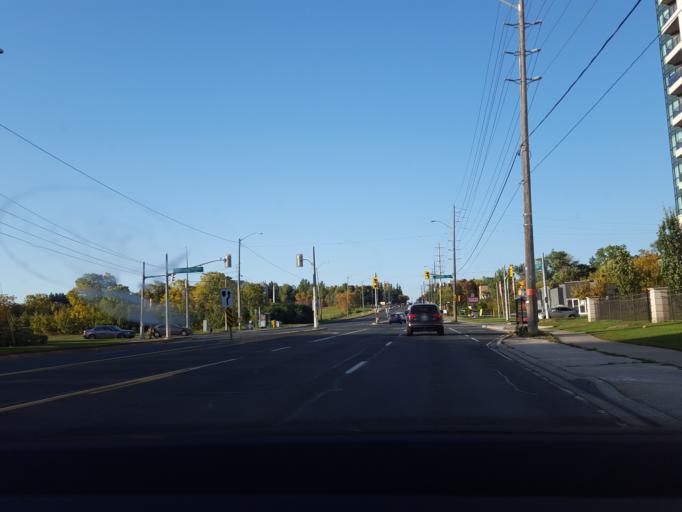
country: CA
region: Ontario
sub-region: York
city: Richmond Hill
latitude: 43.8660
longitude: -79.4360
